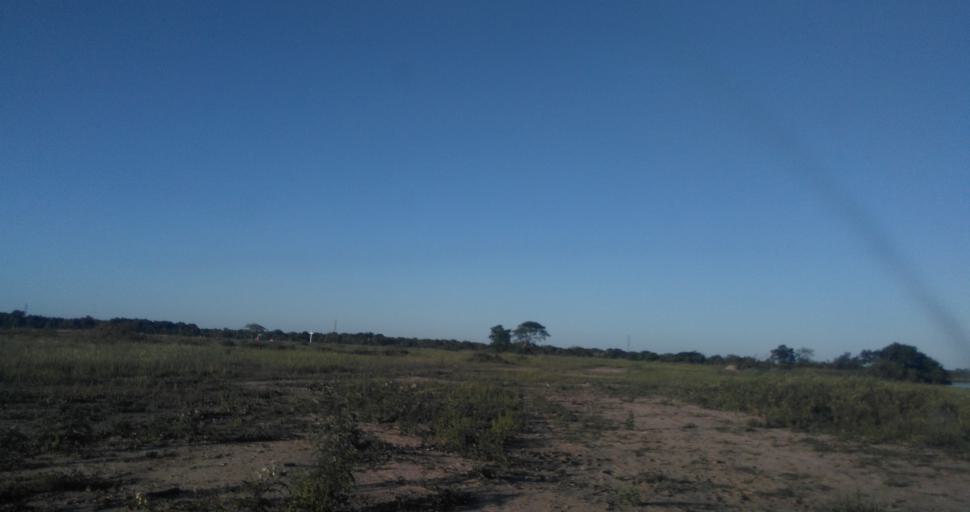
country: AR
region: Chaco
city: Fontana
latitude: -27.3952
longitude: -58.9836
